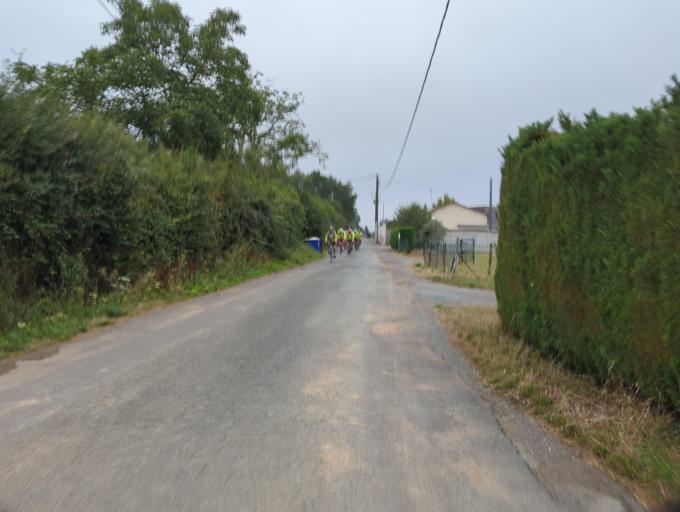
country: FR
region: Pays de la Loire
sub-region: Departement de Maine-et-Loire
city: Trelaze
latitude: 47.4770
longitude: -0.4883
